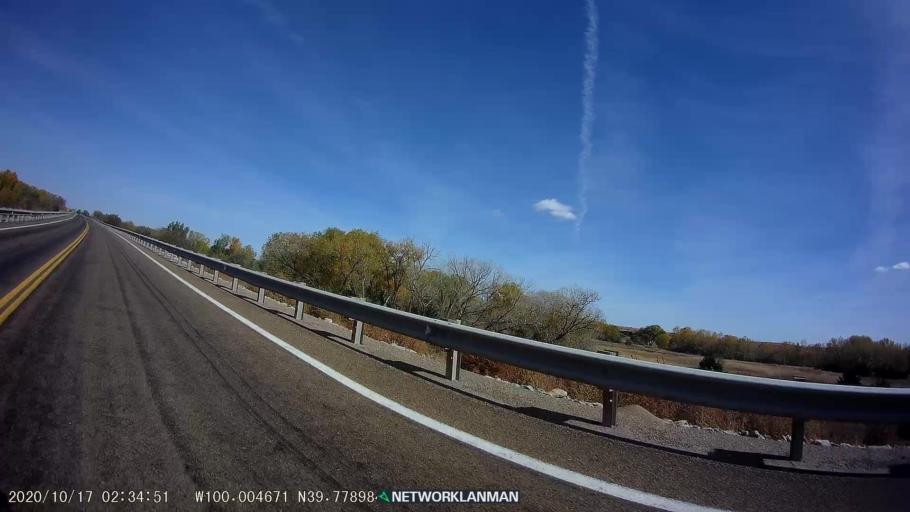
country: US
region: Kansas
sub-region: Norton County
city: Norton
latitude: 39.7797
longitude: -100.0042
